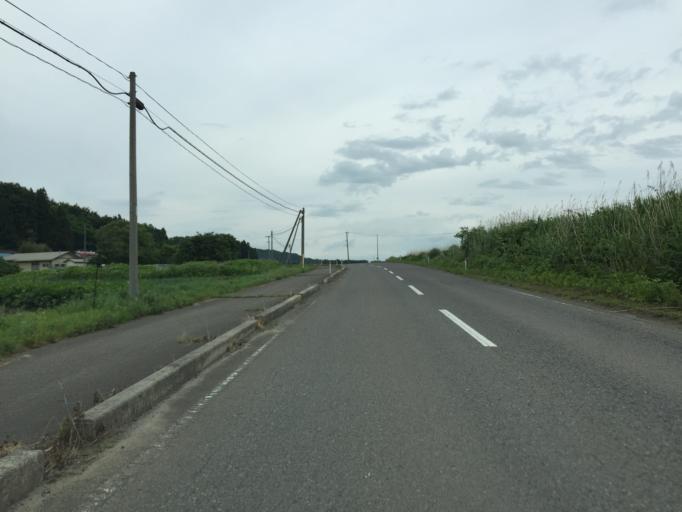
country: JP
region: Fukushima
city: Funehikimachi-funehiki
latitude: 37.3888
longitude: 140.5581
